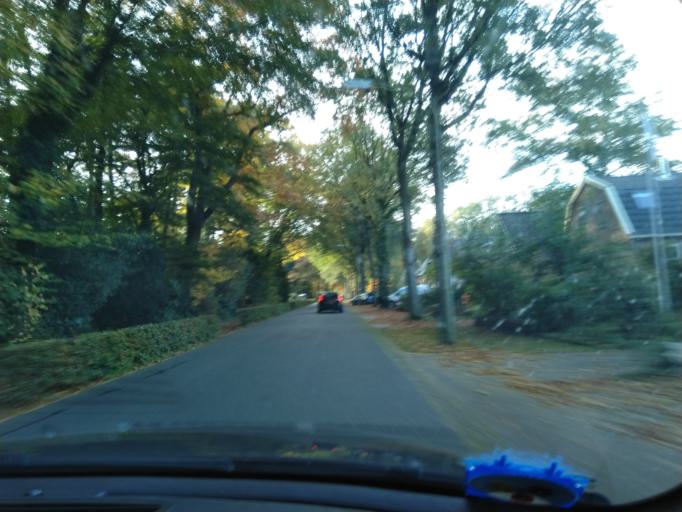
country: NL
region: Drenthe
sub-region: Gemeente Tynaarlo
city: Tynaarlo
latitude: 53.0739
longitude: 6.6316
